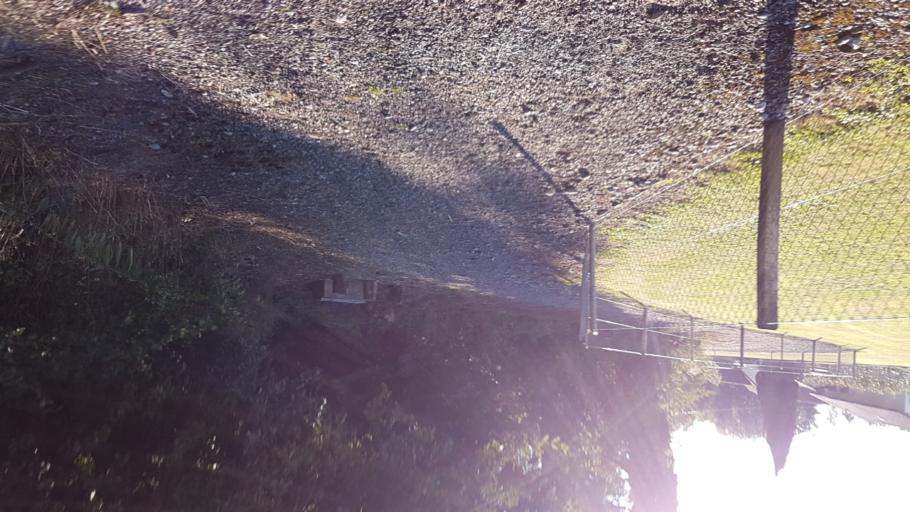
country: CH
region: Bern
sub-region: Bern-Mittelland District
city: Rubigen
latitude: 46.9090
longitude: 7.5352
